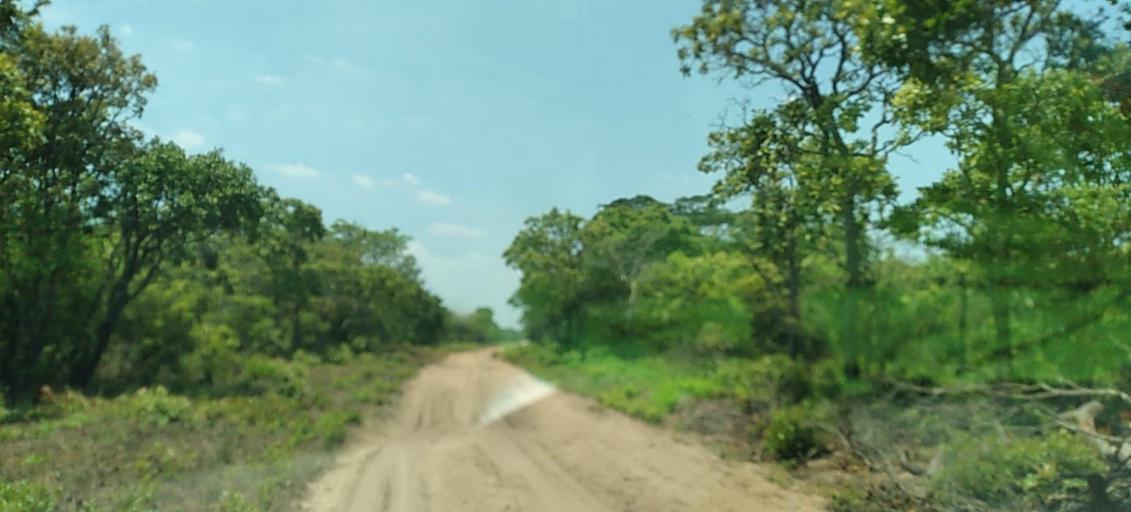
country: CD
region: Katanga
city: Kolwezi
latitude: -11.3397
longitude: 25.2203
